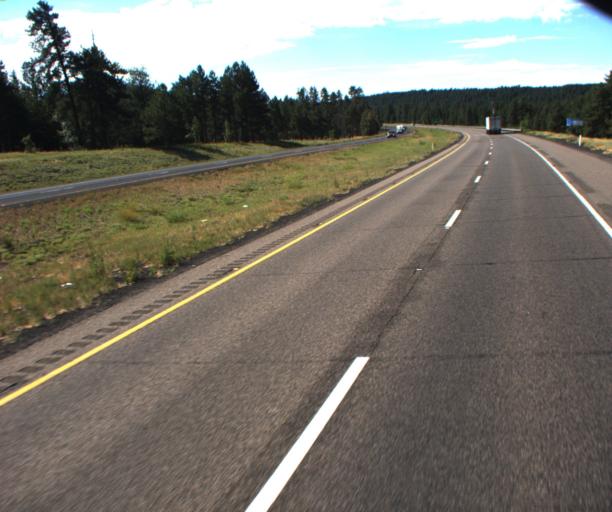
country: US
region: Arizona
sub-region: Coconino County
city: Sedona
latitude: 34.8889
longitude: -111.6419
